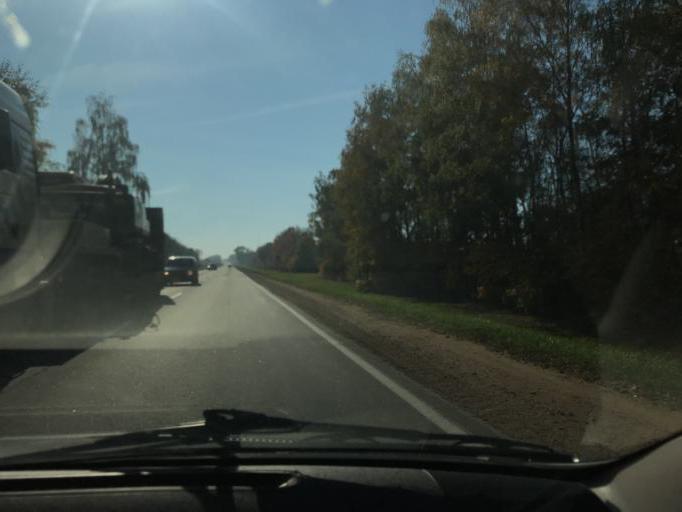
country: BY
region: Minsk
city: Salihorsk
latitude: 52.8078
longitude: 27.4649
